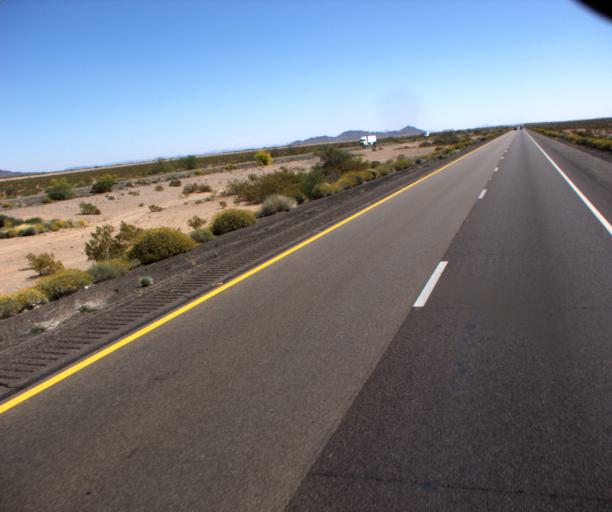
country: US
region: Arizona
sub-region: La Paz County
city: Salome
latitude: 33.5999
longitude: -113.5604
